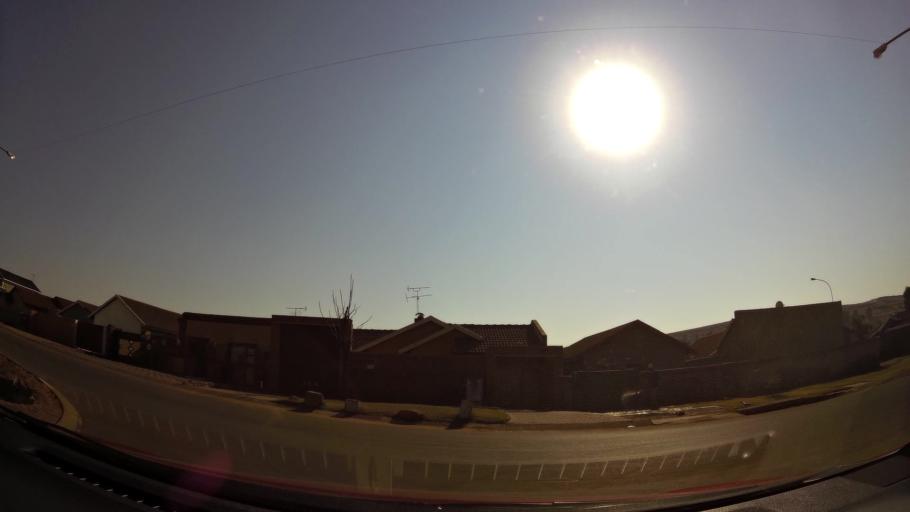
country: ZA
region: Gauteng
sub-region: City of Johannesburg Metropolitan Municipality
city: Johannesburg
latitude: -26.2482
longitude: 27.9617
